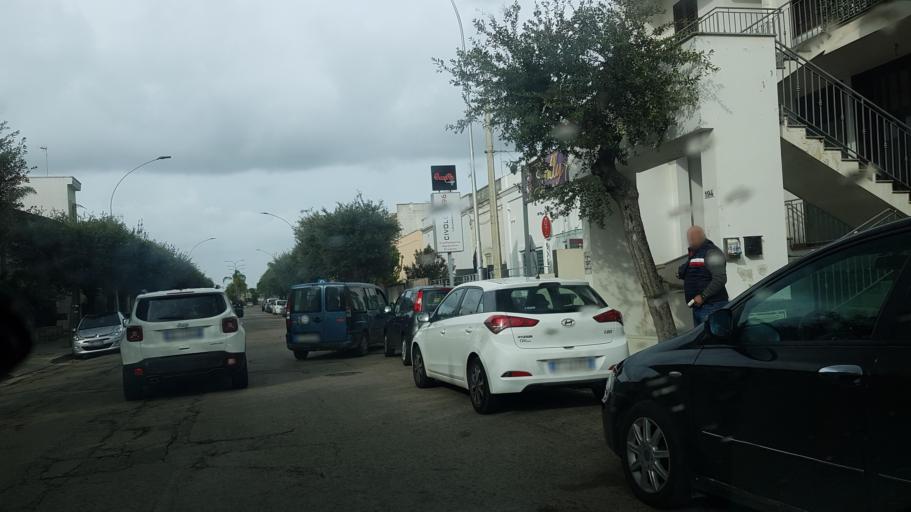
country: IT
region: Apulia
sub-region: Provincia di Lecce
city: Carmiano
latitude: 40.3495
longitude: 18.0405
